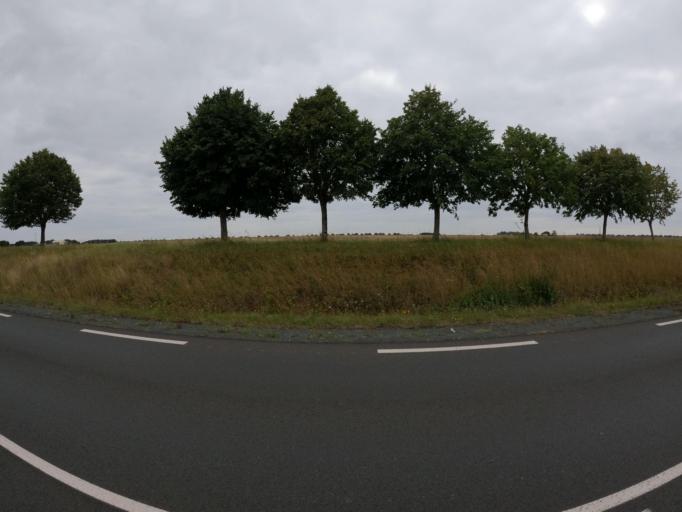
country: FR
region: Pays de la Loire
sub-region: Departement de la Vendee
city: Saint-Michel-le-Cloucq
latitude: 46.4447
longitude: -0.7660
